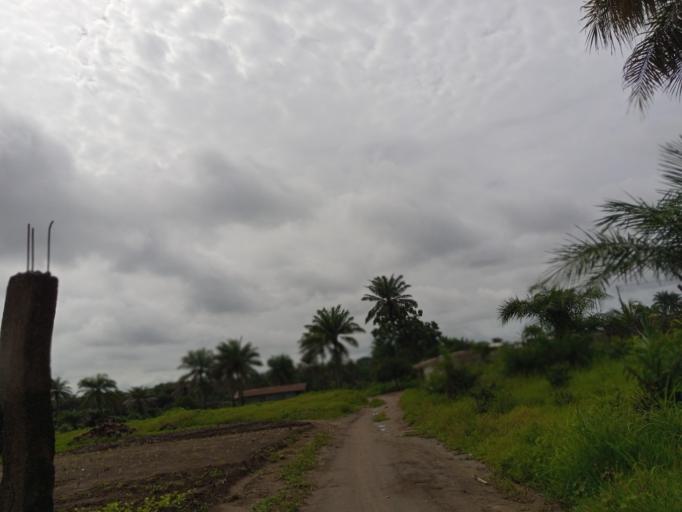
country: SL
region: Northern Province
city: Sawkta
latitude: 8.6253
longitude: -13.1976
